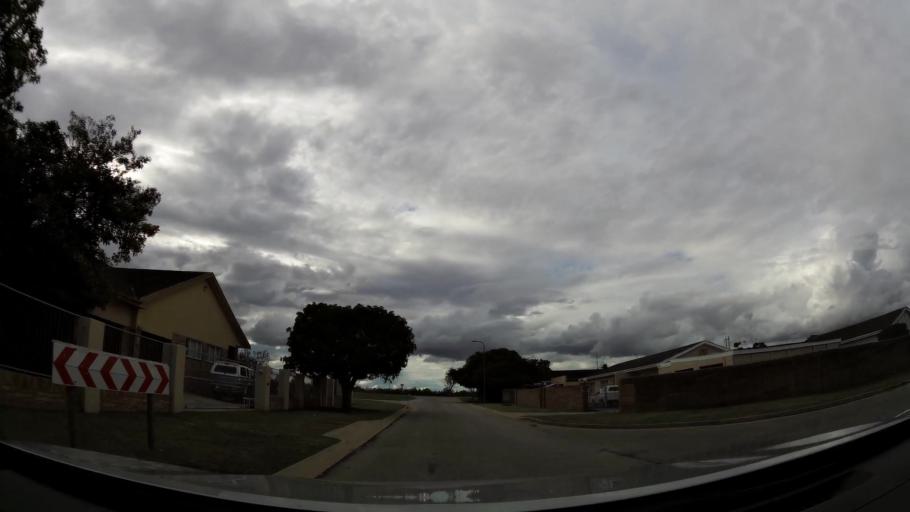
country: ZA
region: Eastern Cape
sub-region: Nelson Mandela Bay Metropolitan Municipality
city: Port Elizabeth
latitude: -33.9366
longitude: 25.4739
